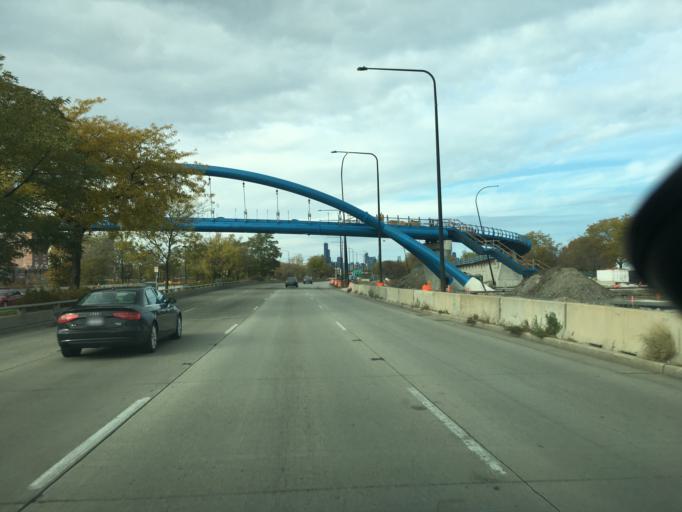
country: US
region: Illinois
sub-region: Cook County
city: Chicago
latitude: 41.8202
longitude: -87.5974
